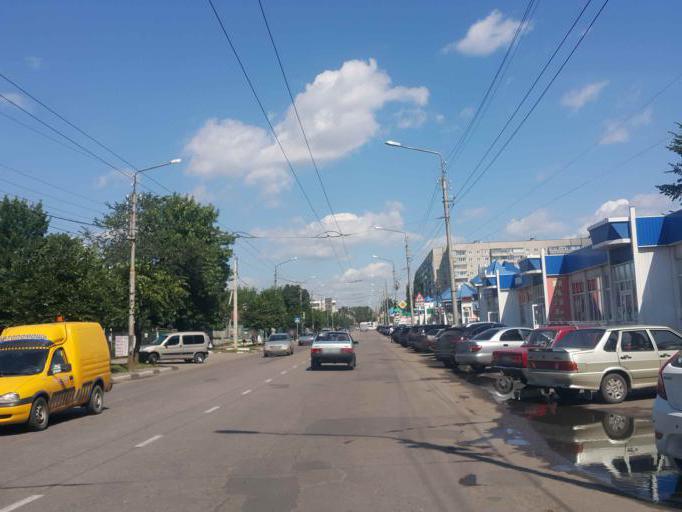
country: RU
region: Tambov
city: Tambov
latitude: 52.7304
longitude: 41.4421
